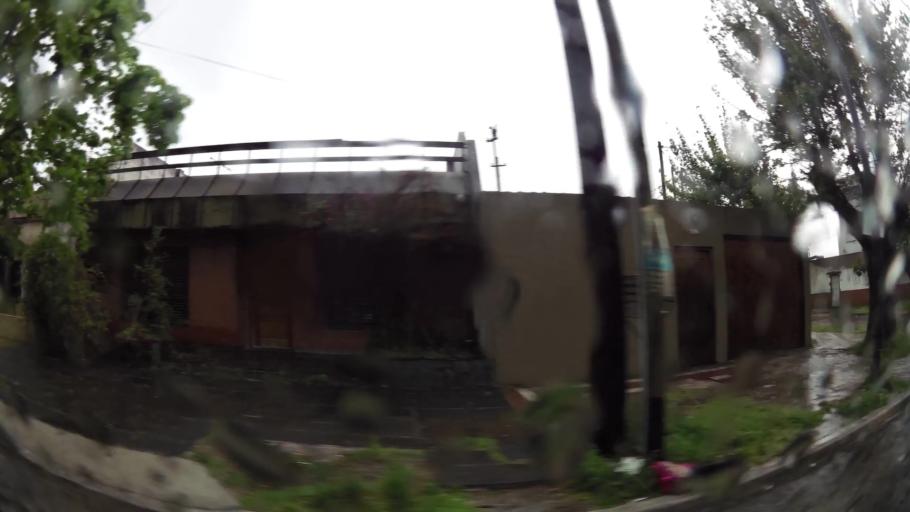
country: AR
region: Buenos Aires
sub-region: Partido de Lanus
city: Lanus
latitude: -34.7139
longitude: -58.4091
